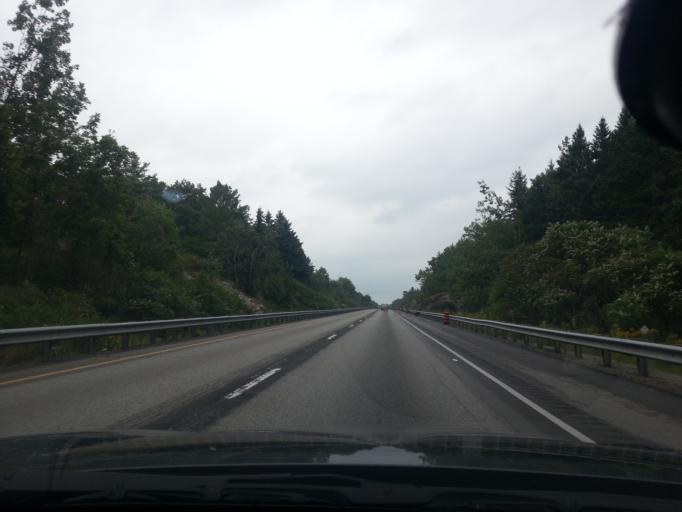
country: US
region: New York
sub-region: Jefferson County
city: Alexandria Bay
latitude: 44.4054
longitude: -75.9312
